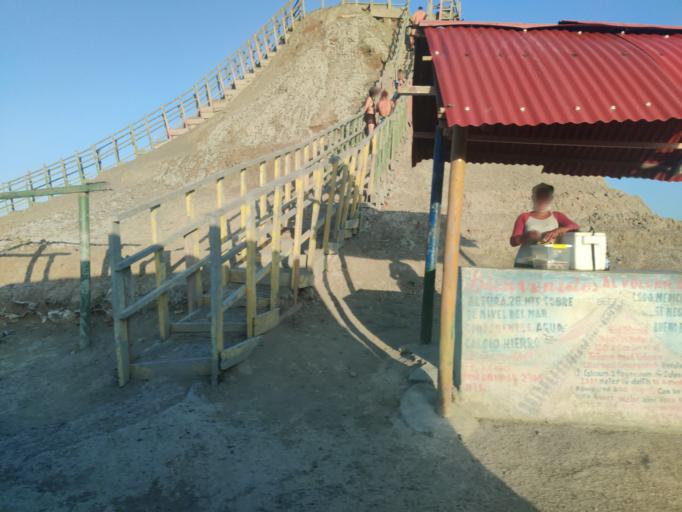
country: CO
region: Atlantico
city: Piojo
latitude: 10.7446
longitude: -75.2414
